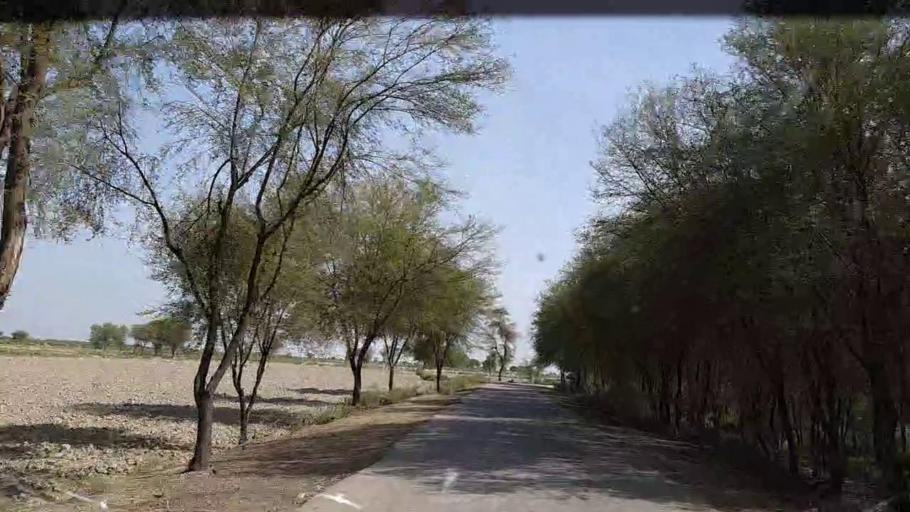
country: PK
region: Sindh
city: Phulji
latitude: 26.9252
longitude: 67.6818
